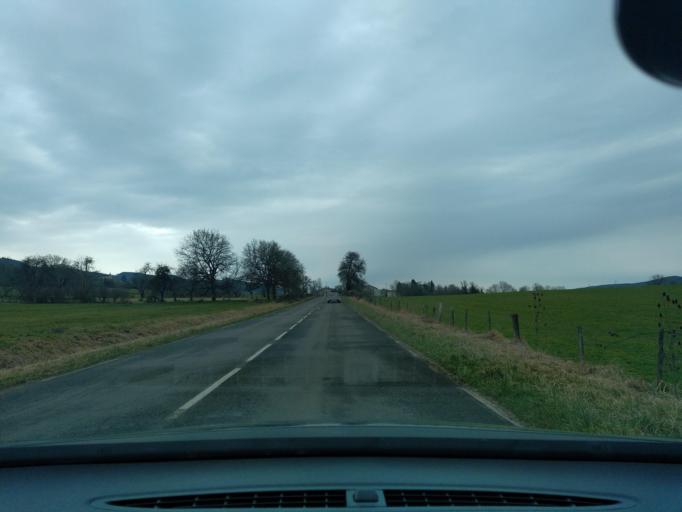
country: FR
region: Franche-Comte
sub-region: Departement du Jura
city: Arinthod
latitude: 46.3853
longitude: 5.5644
